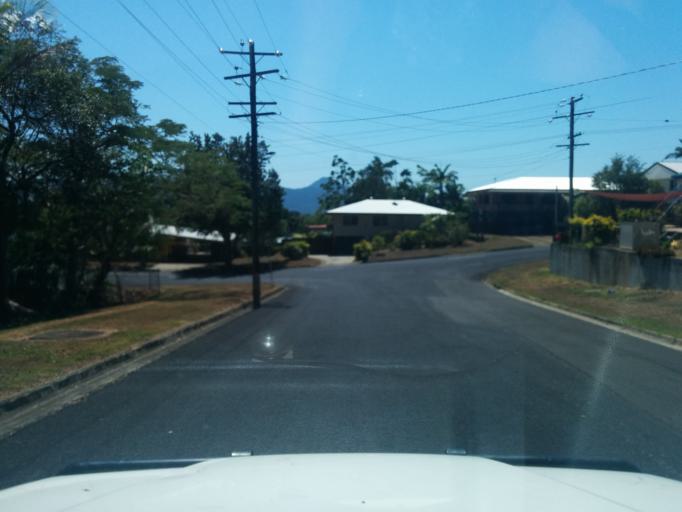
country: AU
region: Queensland
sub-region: Cairns
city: Woree
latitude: -16.9599
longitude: 145.7252
